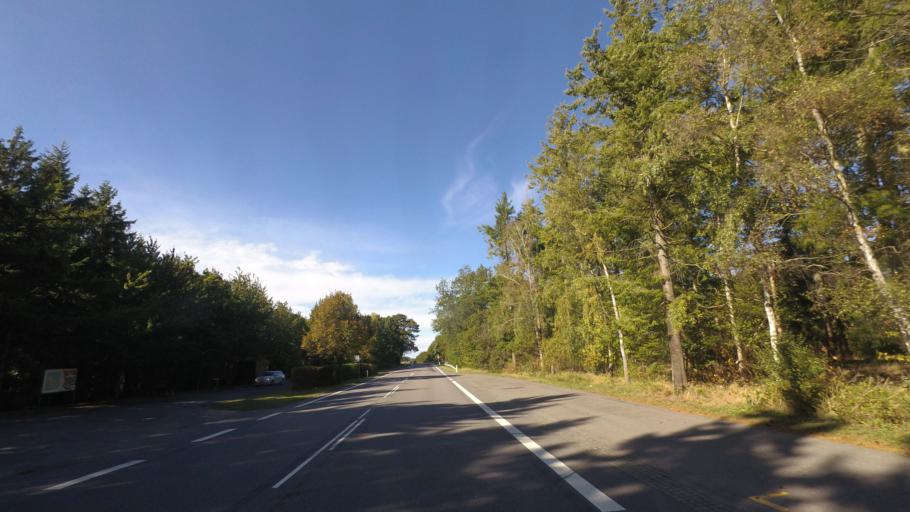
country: DK
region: Capital Region
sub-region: Bornholm Kommune
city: Ronne
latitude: 55.0840
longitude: 14.7496
